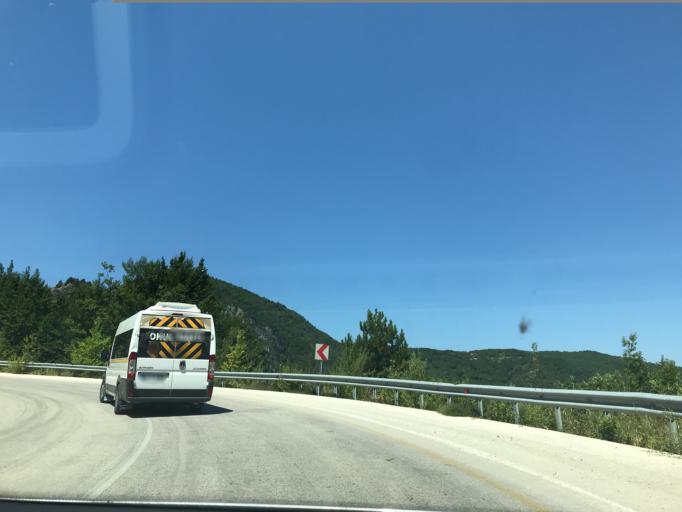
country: TR
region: Bursa
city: Tahtakopru
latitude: 39.9425
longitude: 29.5994
